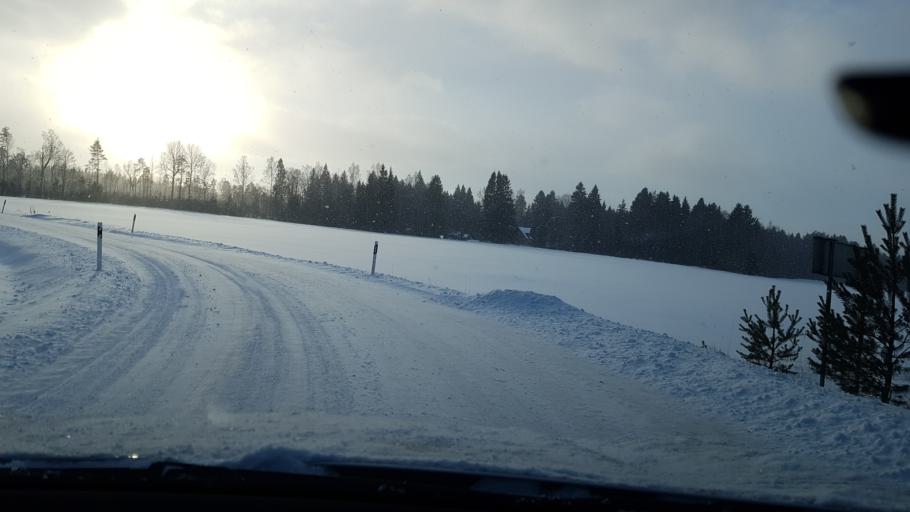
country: EE
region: Harju
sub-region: Nissi vald
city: Turba
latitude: 59.1978
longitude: 24.1390
